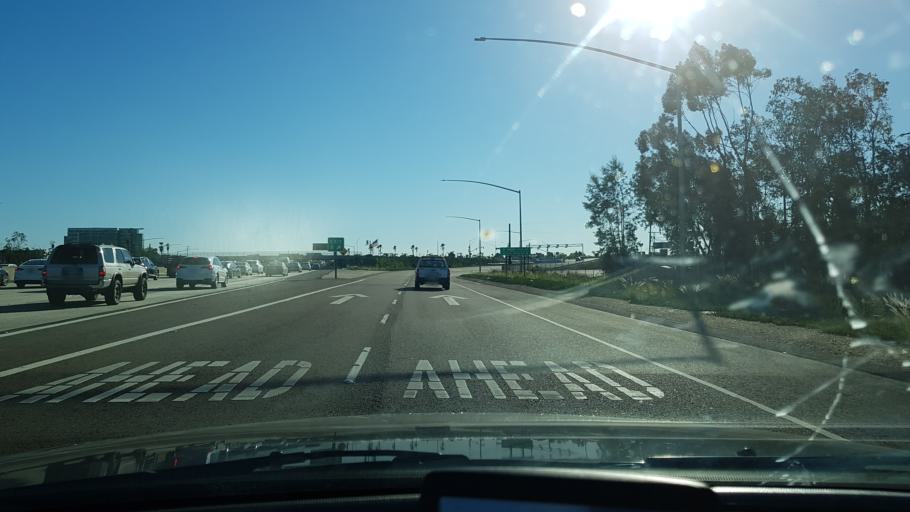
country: US
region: California
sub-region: San Diego County
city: San Diego
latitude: 32.8353
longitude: -117.1390
